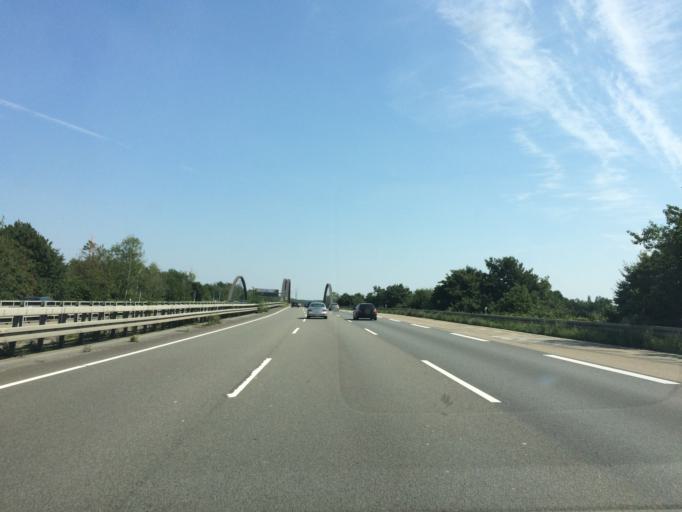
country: DE
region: North Rhine-Westphalia
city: Waltrop
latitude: 51.5835
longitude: 7.4036
